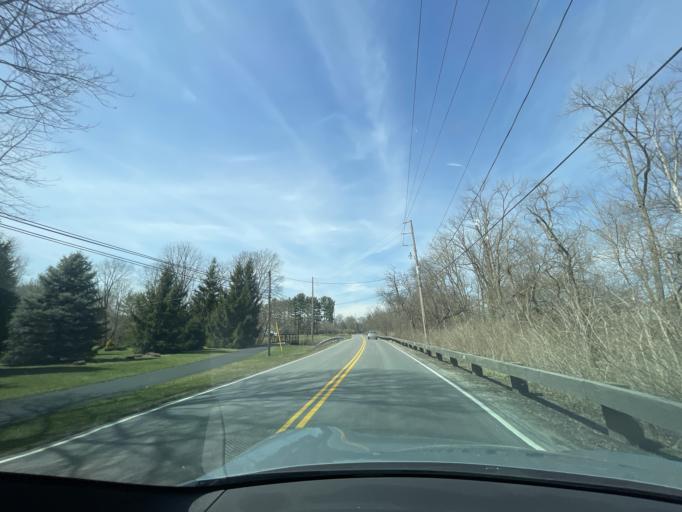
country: US
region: Ohio
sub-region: Franklin County
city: Dublin
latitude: 40.1230
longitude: -83.1377
